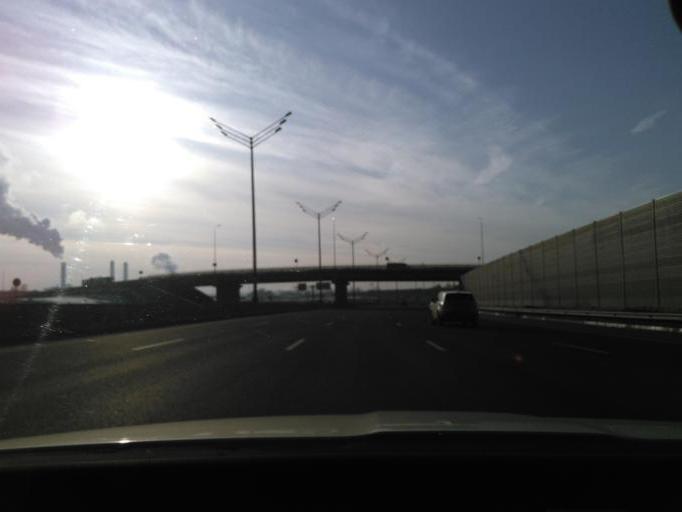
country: RU
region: Moskovskaya
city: Levoberezhnaya
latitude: 55.9015
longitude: 37.4845
